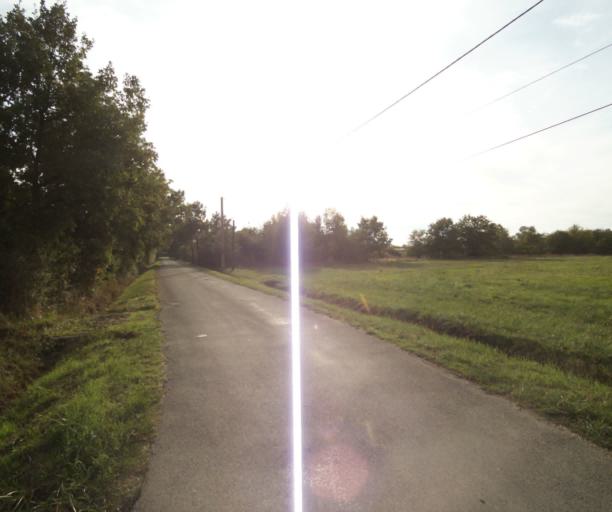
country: FR
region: Midi-Pyrenees
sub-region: Departement du Tarn-et-Garonne
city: Campsas
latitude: 43.8764
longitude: 1.3203
